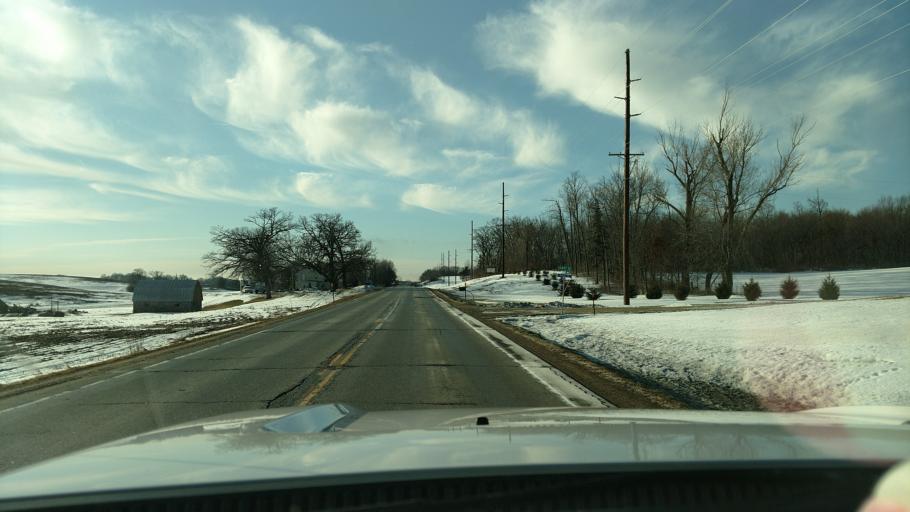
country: US
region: Minnesota
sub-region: Wabasha County
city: Lake City
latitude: 44.3174
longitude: -92.4109
